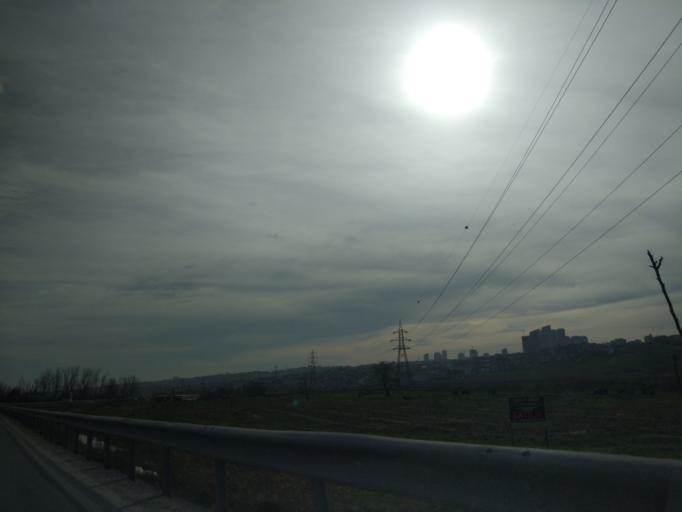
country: TR
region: Istanbul
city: Esenyurt
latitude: 41.0558
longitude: 28.7015
